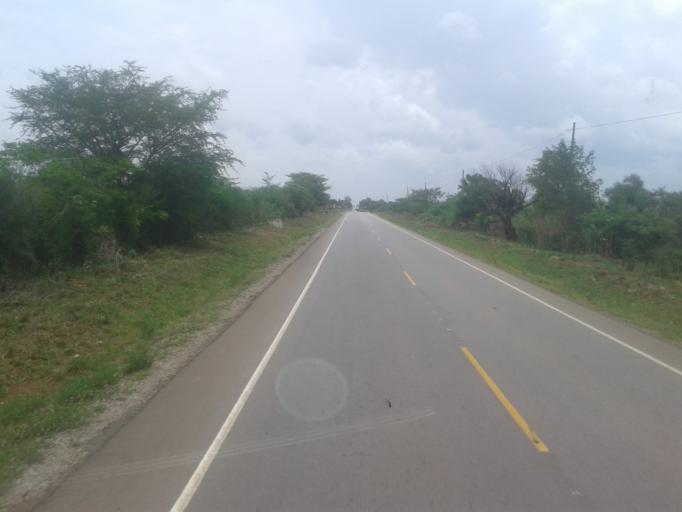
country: UG
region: Western Region
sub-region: Kiryandongo District
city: Masindi Port
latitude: 1.6369
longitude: 32.0317
